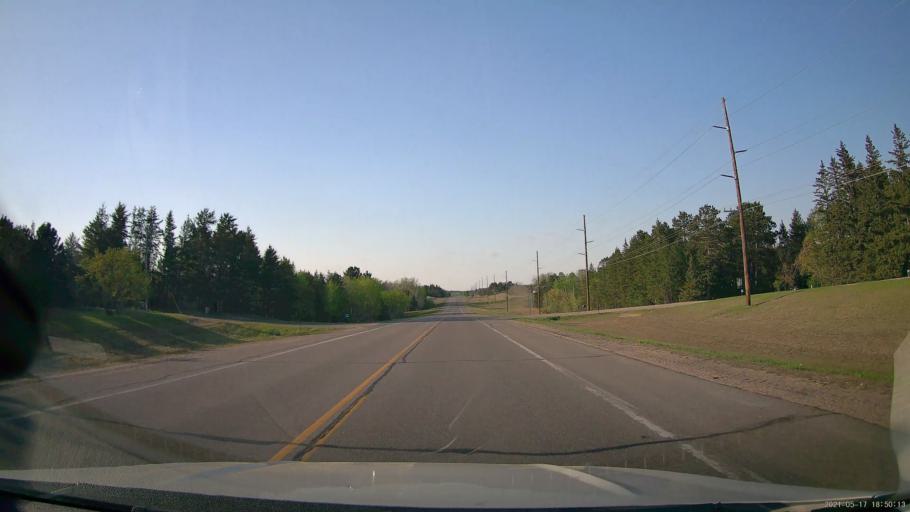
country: US
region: Minnesota
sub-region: Hubbard County
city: Park Rapids
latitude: 46.9310
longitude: -95.0168
